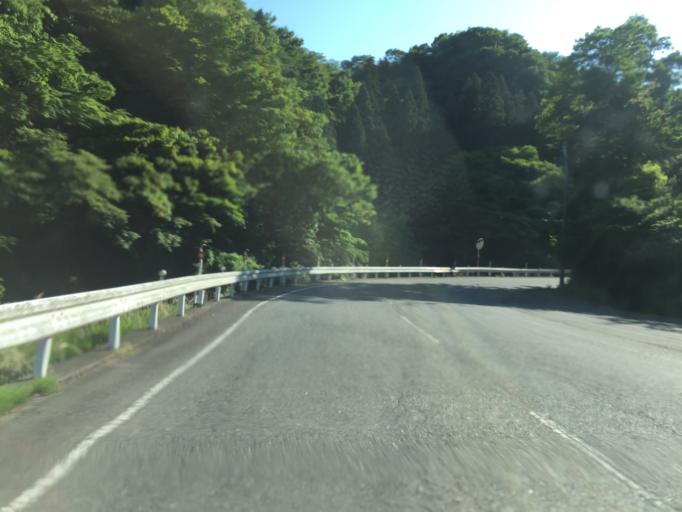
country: JP
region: Ibaraki
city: Kitaibaraki
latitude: 36.8634
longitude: 140.6516
